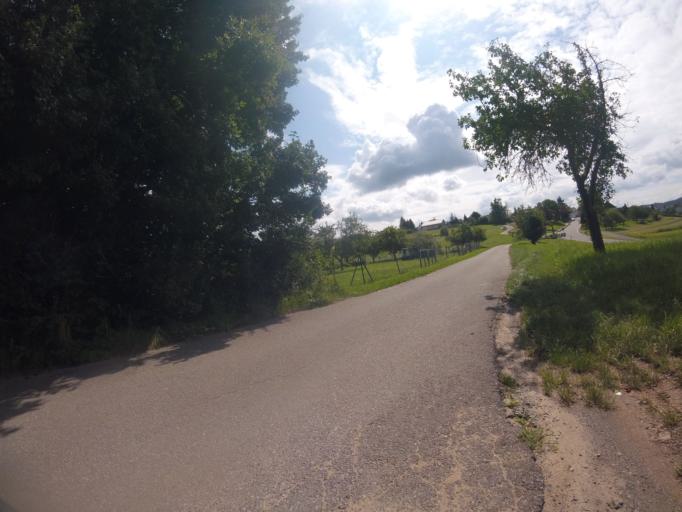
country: DE
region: Baden-Wuerttemberg
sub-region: Regierungsbezirk Stuttgart
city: Winnenden
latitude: 48.8573
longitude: 9.4059
